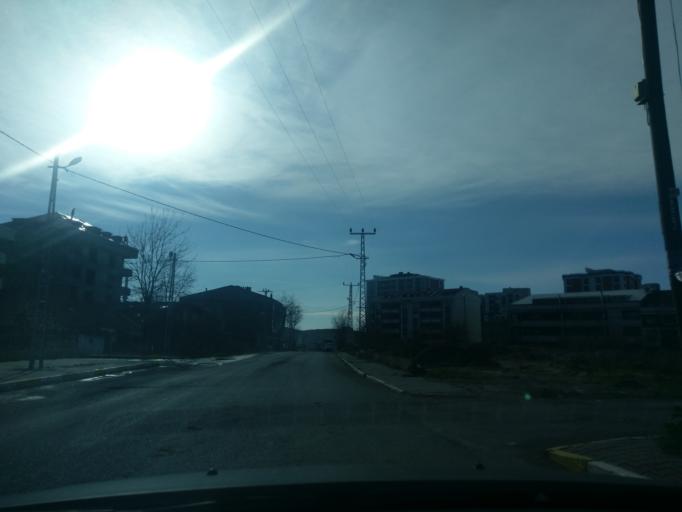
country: TR
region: Istanbul
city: Sultangazi
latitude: 41.1315
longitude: 28.8381
